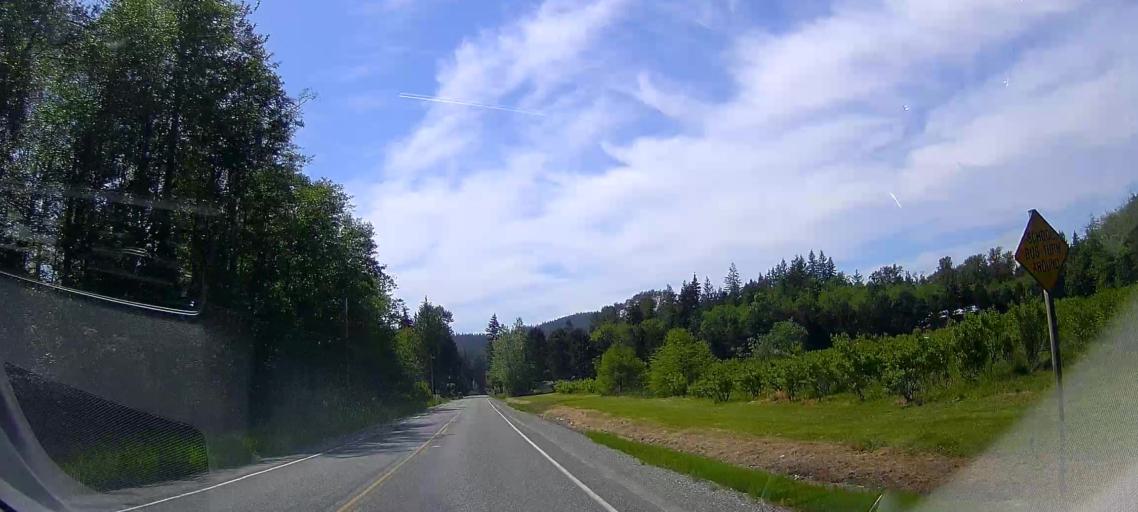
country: US
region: Washington
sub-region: Skagit County
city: Big Lake
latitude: 48.3950
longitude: -122.2736
